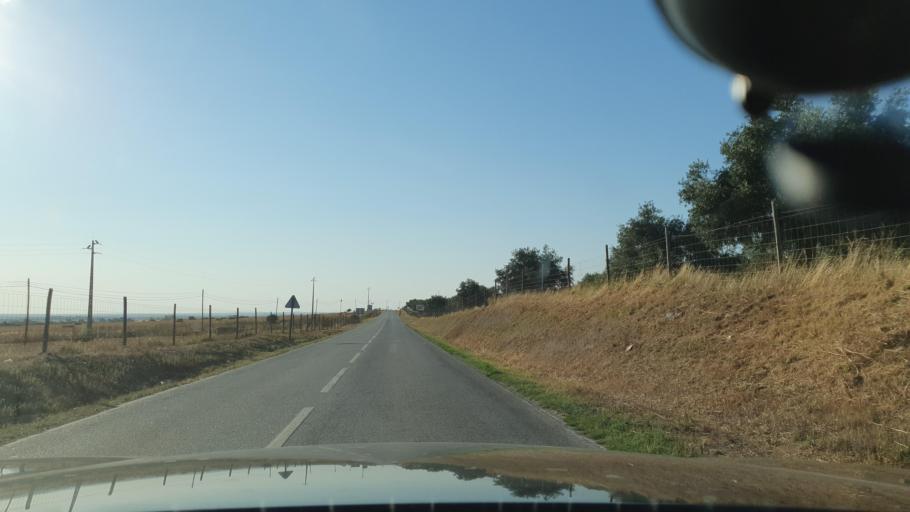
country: PT
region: Evora
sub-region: Estremoz
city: Estremoz
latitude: 38.8788
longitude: -7.6399
